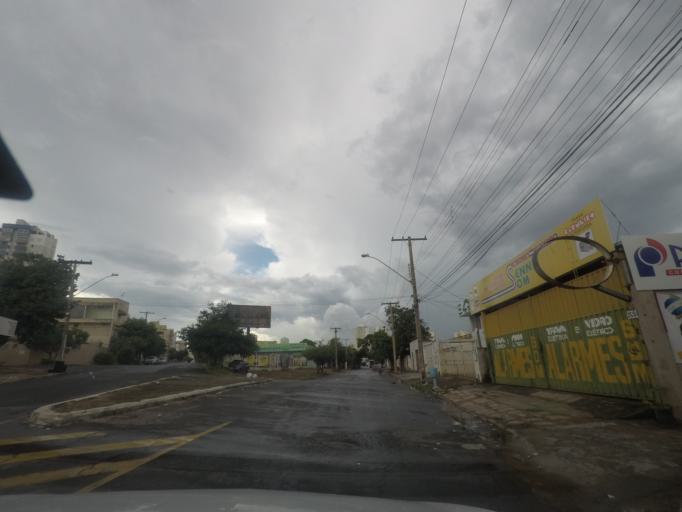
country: BR
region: Goias
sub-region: Goiania
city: Goiania
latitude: -16.6719
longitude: -49.2752
